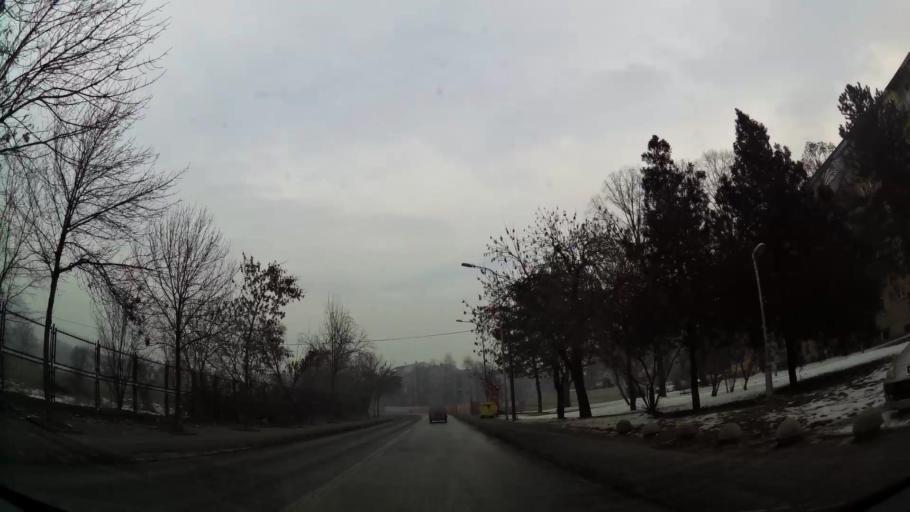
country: MK
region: Cair
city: Cair
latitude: 42.0052
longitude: 21.4614
